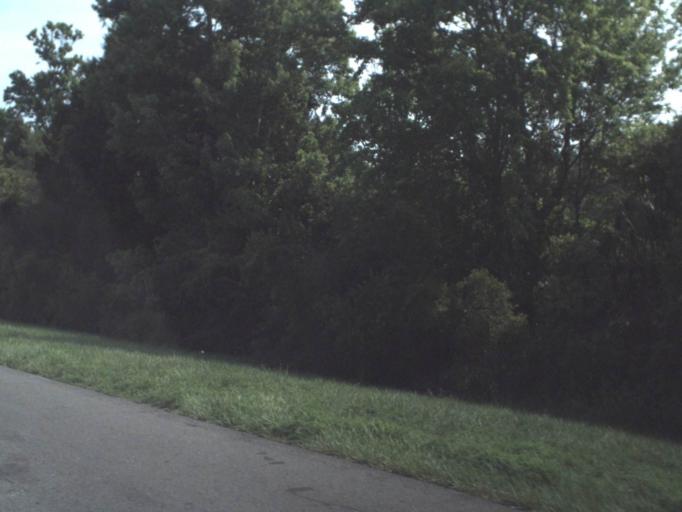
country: US
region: Florida
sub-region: Nassau County
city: Yulee
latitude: 30.5712
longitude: -81.6446
